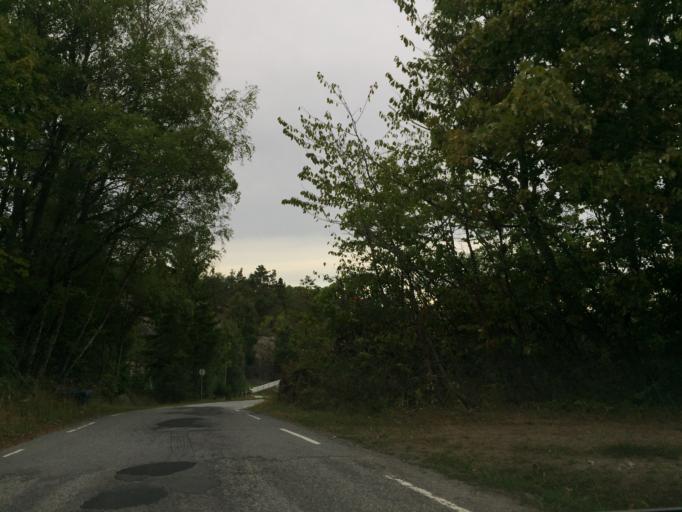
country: NO
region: Ostfold
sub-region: Hvaler
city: Skjaerhalden
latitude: 59.0582
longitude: 11.0363
